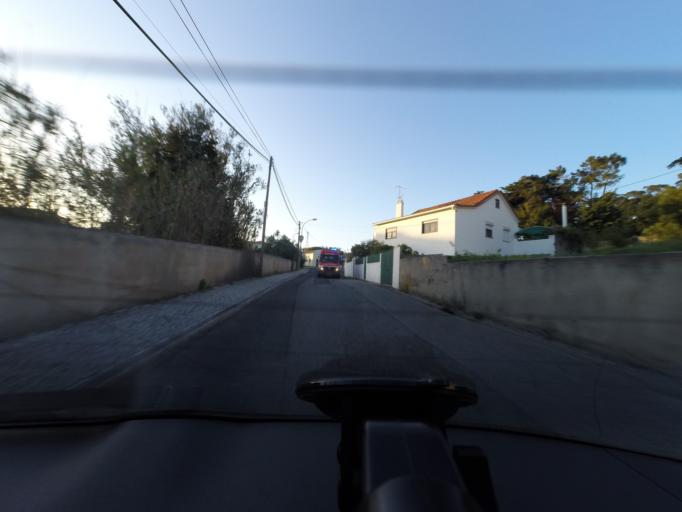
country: PT
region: Lisbon
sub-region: Sintra
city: Rio de Mouro
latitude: 38.7565
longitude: -9.3585
